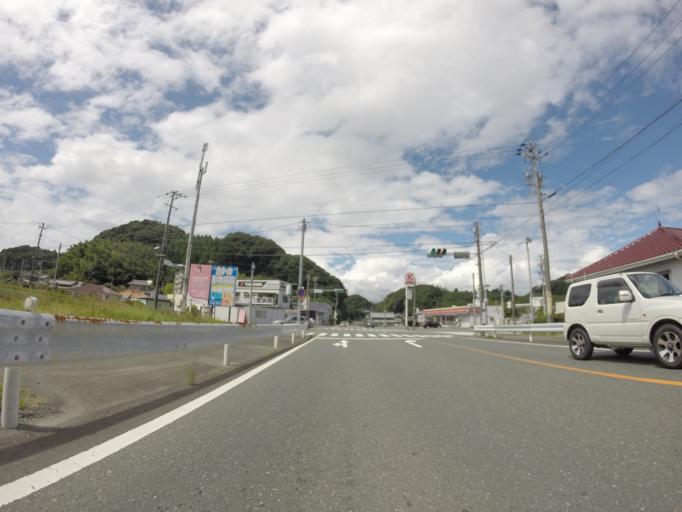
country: JP
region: Shizuoka
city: Kakegawa
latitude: 34.7403
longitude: 138.0406
